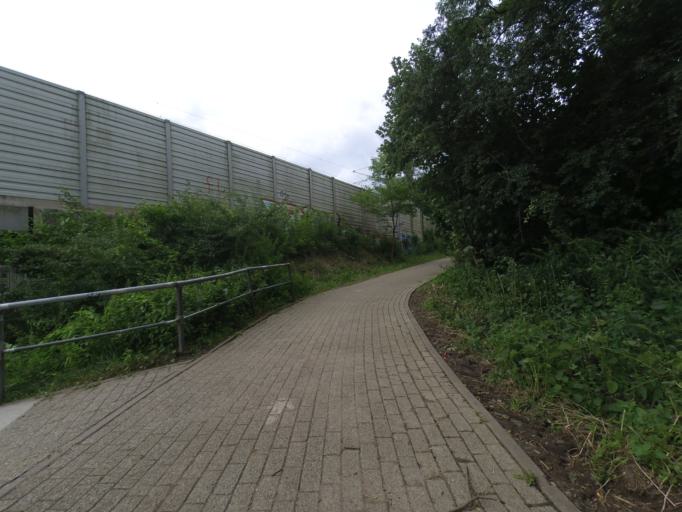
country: DE
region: Hamburg
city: Marienthal
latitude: 53.5535
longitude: 10.0681
